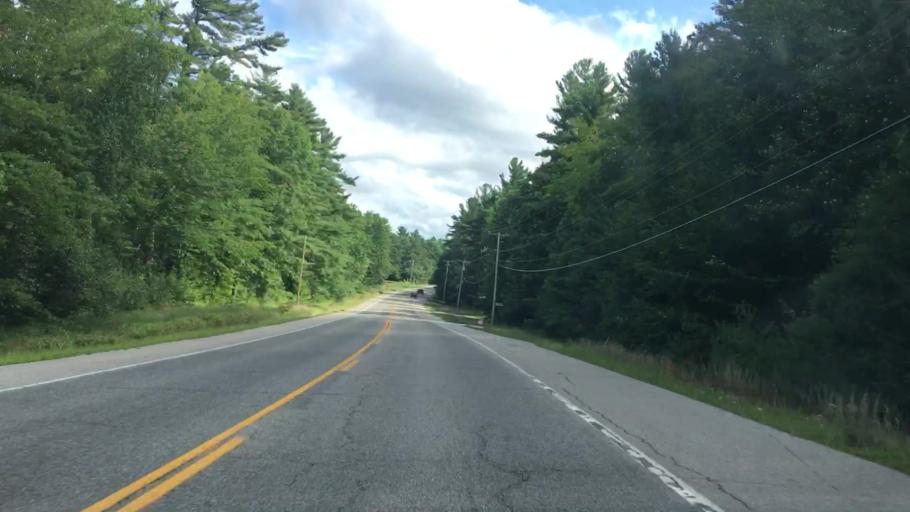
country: US
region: Maine
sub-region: York County
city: South Sanford
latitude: 43.3747
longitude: -70.7383
